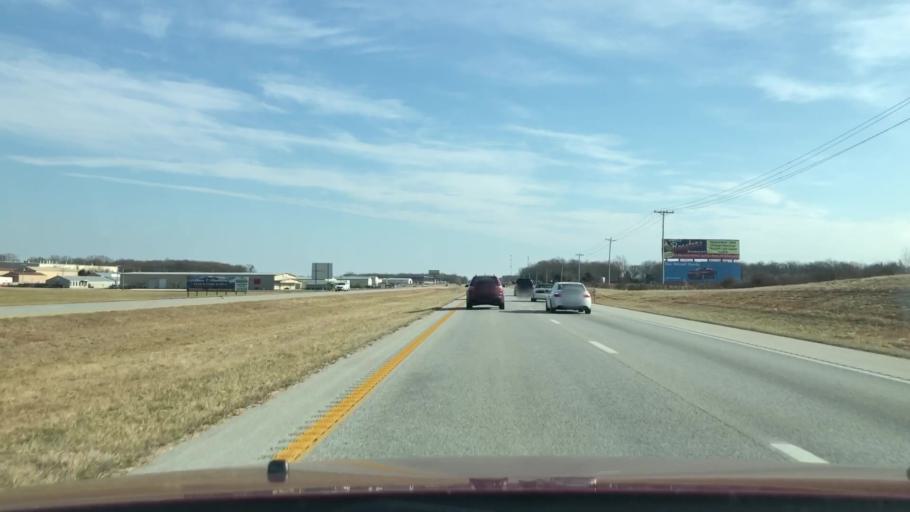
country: US
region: Missouri
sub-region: Webster County
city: Rogersville
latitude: 37.1133
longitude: -93.0417
